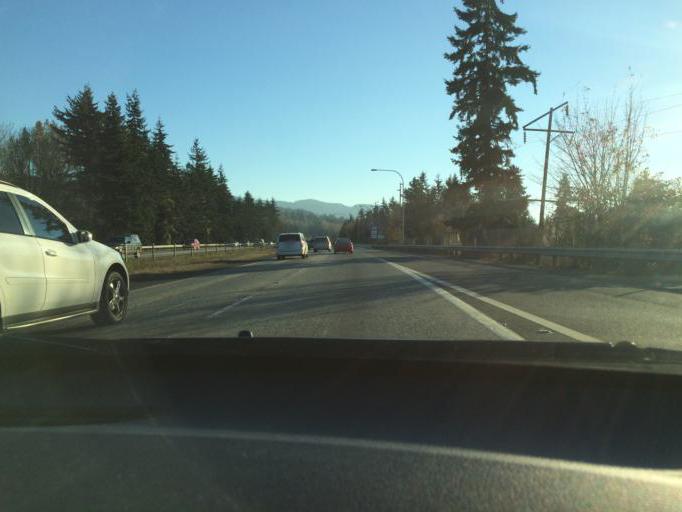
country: US
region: Washington
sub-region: Whatcom County
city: Bellingham
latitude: 48.7425
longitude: -122.4676
